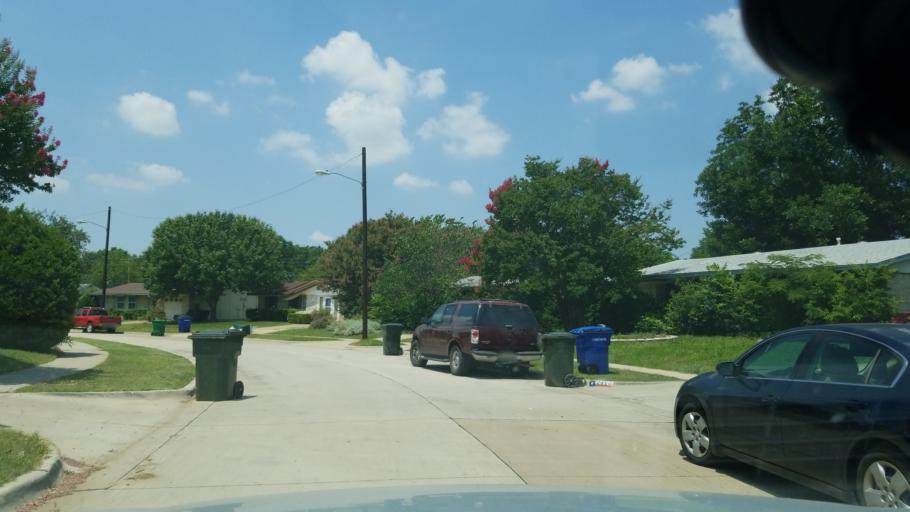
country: US
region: Texas
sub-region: Dallas County
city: Carrollton
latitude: 32.9522
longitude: -96.8751
